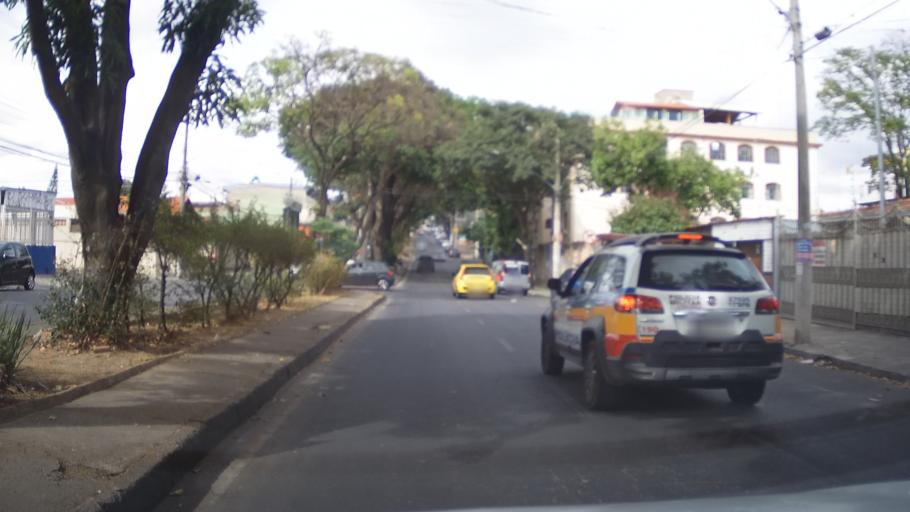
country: BR
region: Minas Gerais
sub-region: Belo Horizonte
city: Belo Horizonte
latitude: -19.8380
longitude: -43.9487
